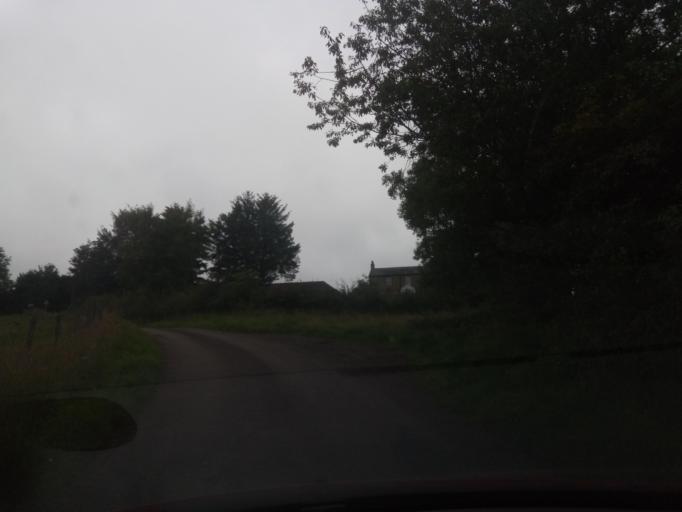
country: GB
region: England
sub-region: Northumberland
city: Otterburn
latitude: 55.2772
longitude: -2.0936
